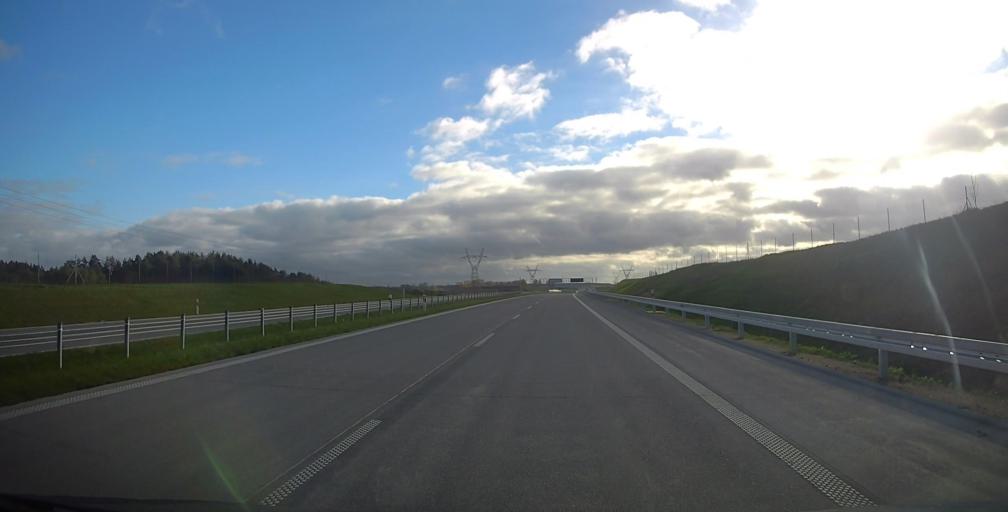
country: PL
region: Podlasie
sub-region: Powiat grajewski
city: Szczuczyn
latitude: 53.6848
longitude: 22.2950
